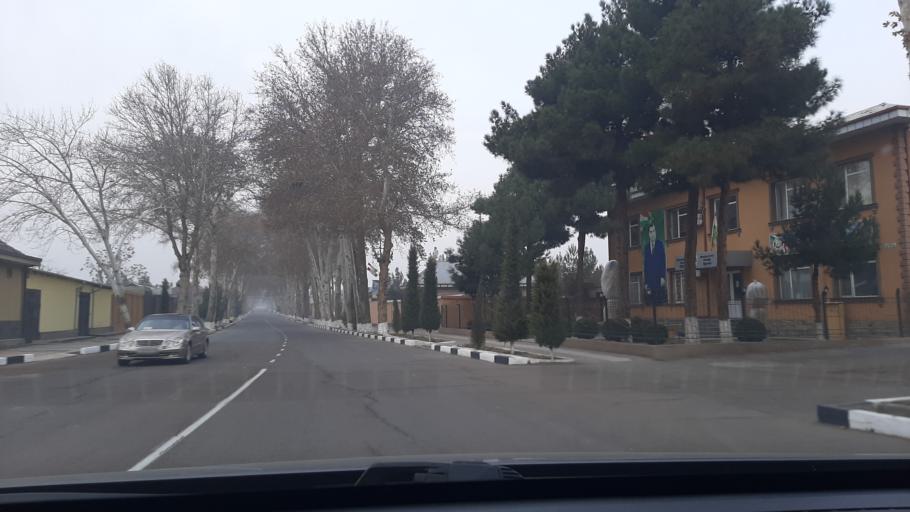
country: TJ
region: Viloyati Sughd
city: Chkalov
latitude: 40.2391
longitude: 69.7004
